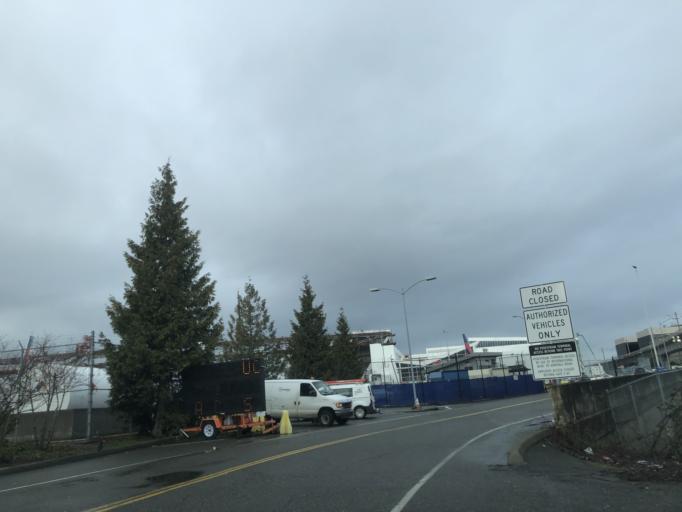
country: US
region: Washington
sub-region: King County
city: SeaTac
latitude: 47.4366
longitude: -122.2976
